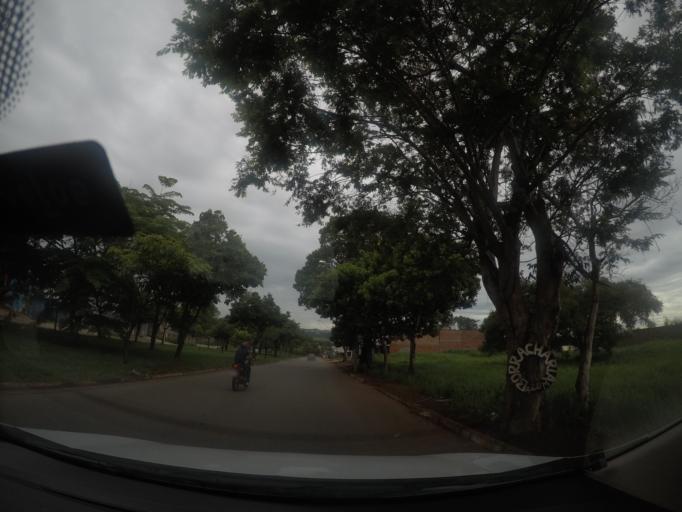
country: BR
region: Goias
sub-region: Goiania
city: Goiania
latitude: -16.6061
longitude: -49.3021
